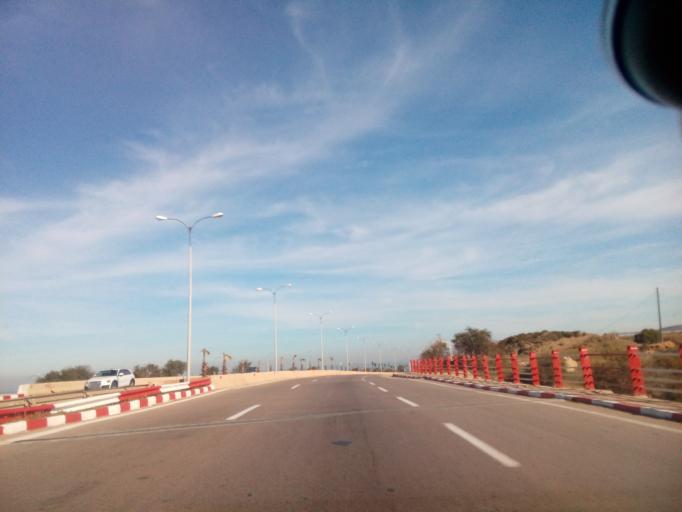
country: DZ
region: Mostaganem
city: Mostaganem
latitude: 35.8328
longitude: -0.0096
